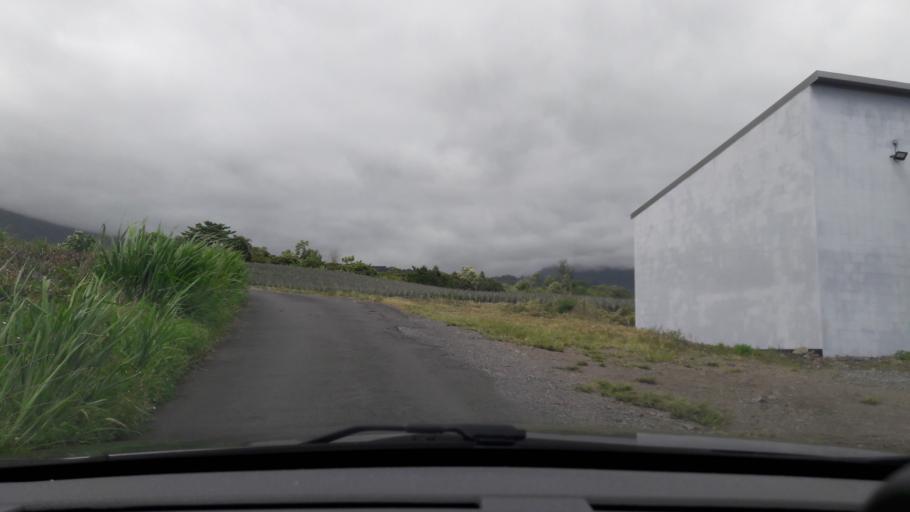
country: RE
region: Reunion
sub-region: Reunion
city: Saint-Benoit
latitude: -21.0958
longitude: 55.7004
